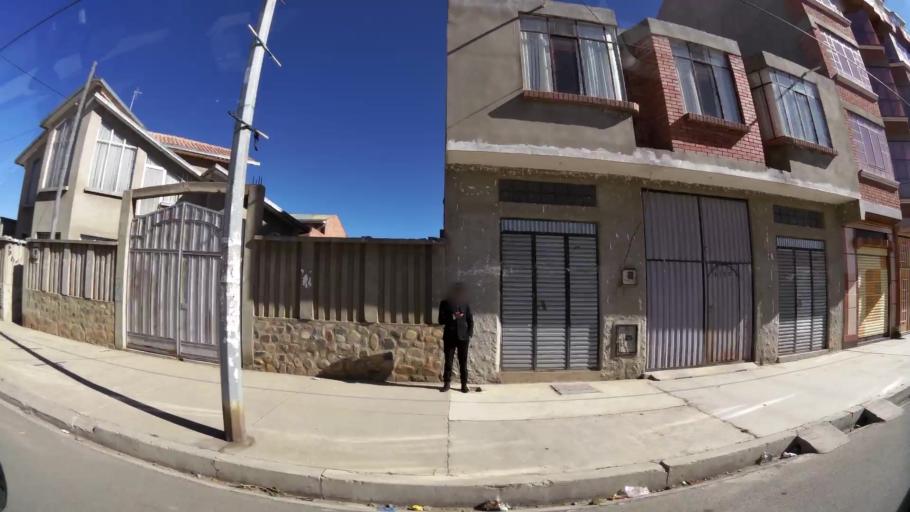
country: BO
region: La Paz
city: La Paz
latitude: -16.5249
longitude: -68.2079
